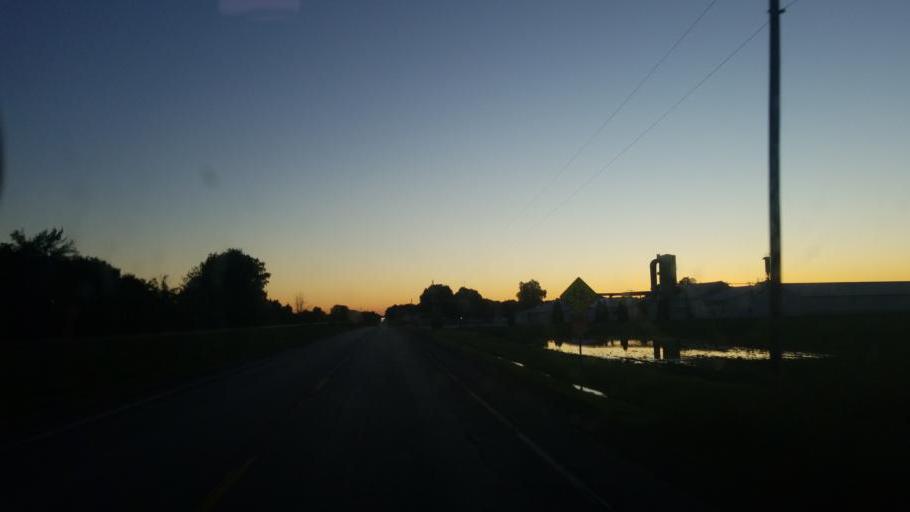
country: US
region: Indiana
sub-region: Elkhart County
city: Nappanee
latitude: 41.4442
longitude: -86.0420
